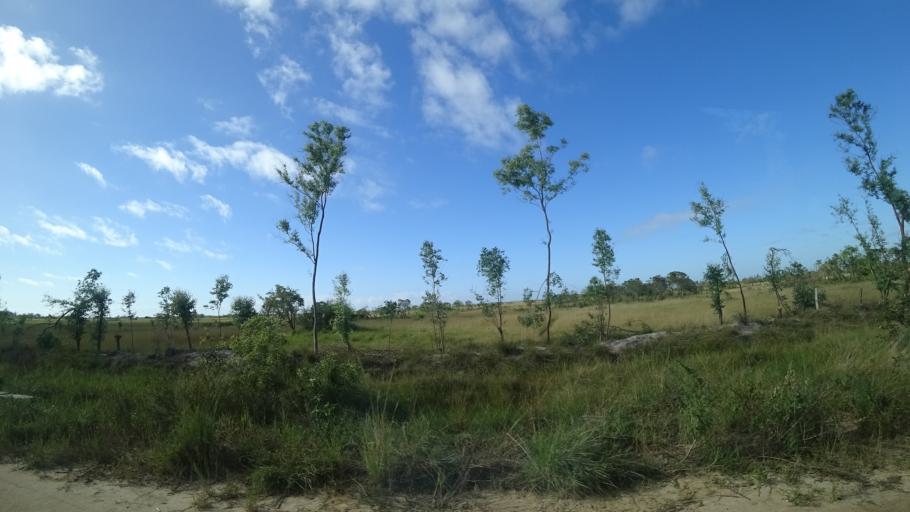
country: MZ
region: Sofala
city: Beira
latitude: -19.7210
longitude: 34.9991
